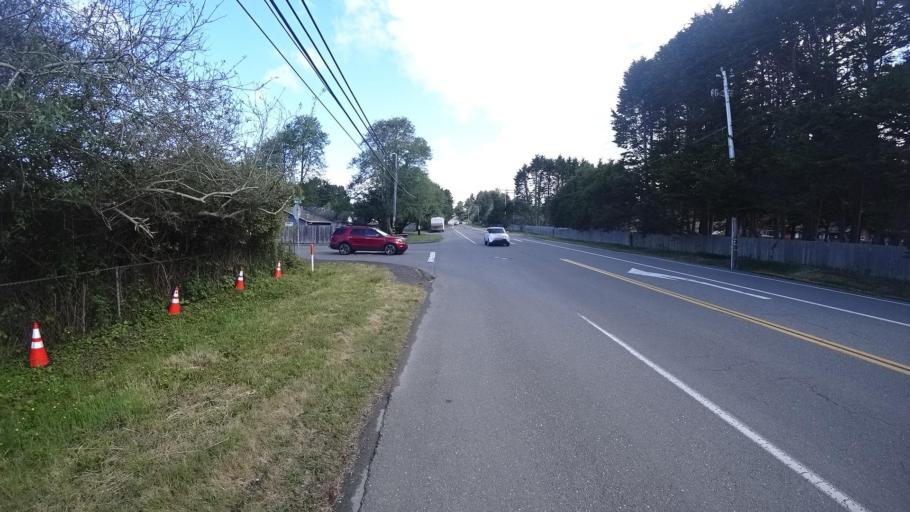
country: US
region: California
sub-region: Humboldt County
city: McKinleyville
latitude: 40.9608
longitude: -124.1009
